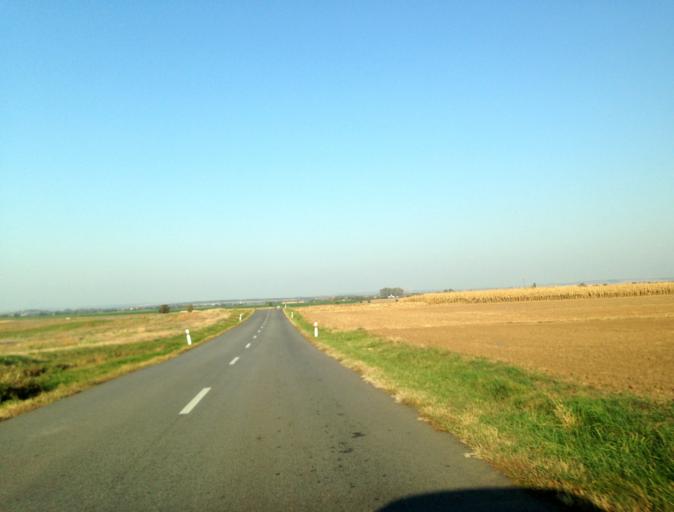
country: SK
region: Nitriansky
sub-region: Okres Komarno
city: Hurbanovo
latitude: 47.9078
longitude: 18.2856
